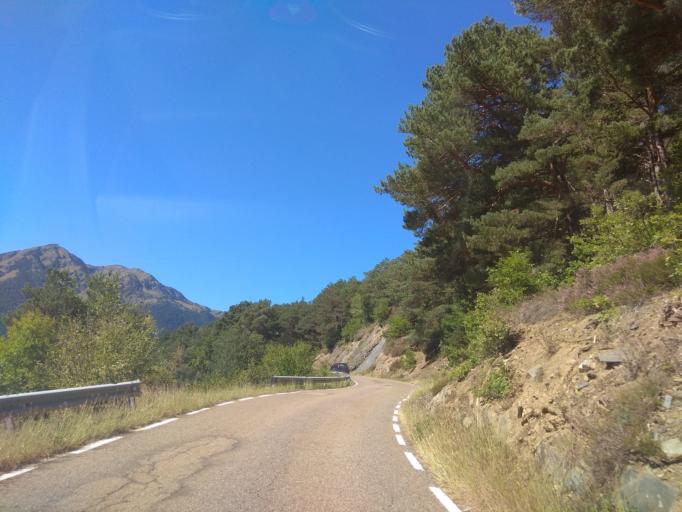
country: ES
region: Catalonia
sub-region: Provincia de Lleida
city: Vielha
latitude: 42.7408
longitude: 0.7500
